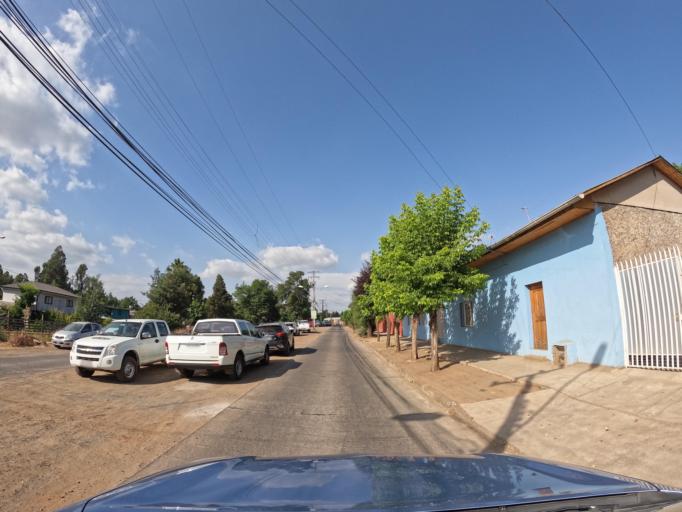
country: CL
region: Maule
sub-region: Provincia de Curico
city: Molina
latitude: -35.2800
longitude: -71.2581
